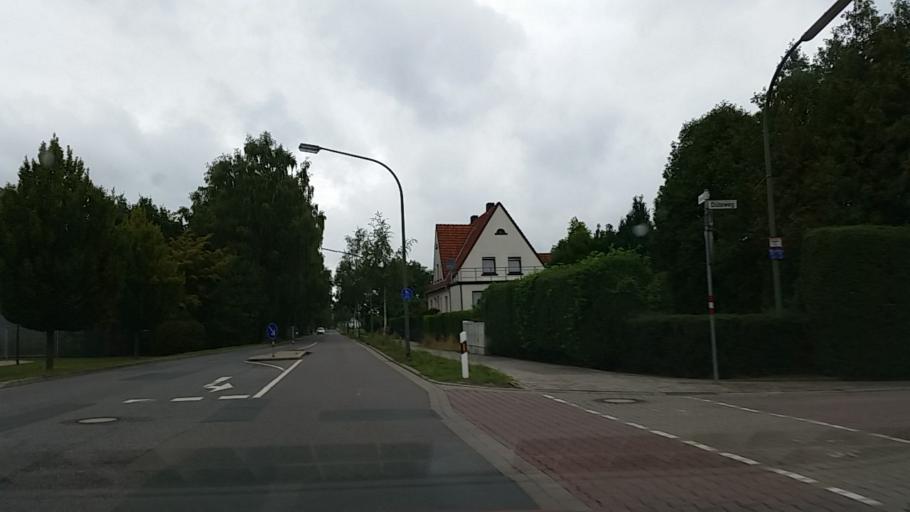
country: DE
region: North Rhine-Westphalia
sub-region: Regierungsbezirk Munster
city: Lotte
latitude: 52.2810
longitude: 7.9504
